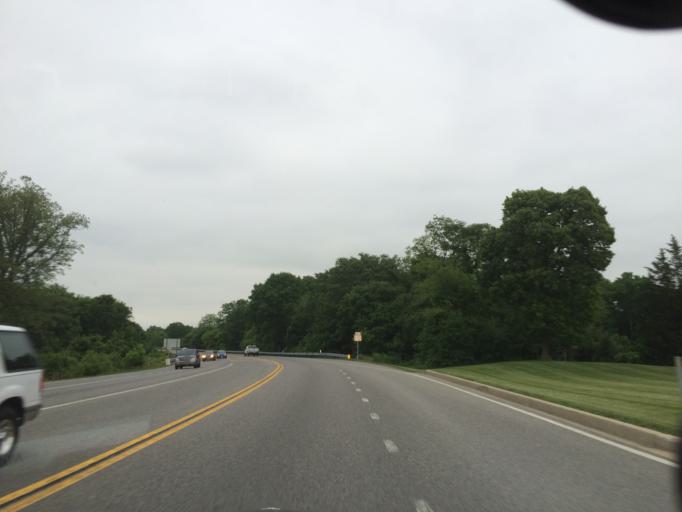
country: US
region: Maryland
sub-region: Washington County
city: Halfway
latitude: 39.6104
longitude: -77.7461
